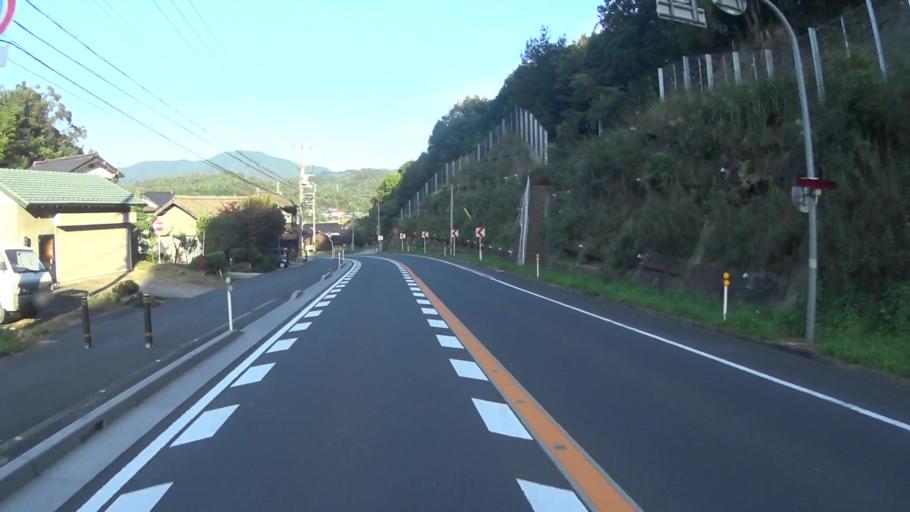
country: JP
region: Hyogo
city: Toyooka
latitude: 35.5837
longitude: 134.9580
